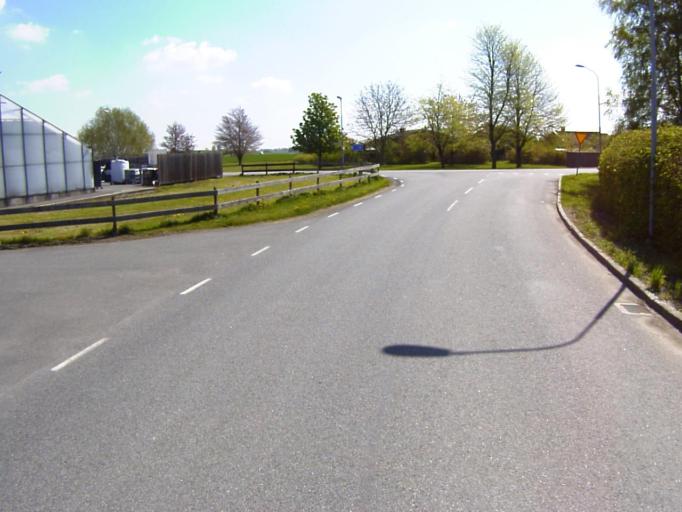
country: SE
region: Skane
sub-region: Kristianstads Kommun
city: Fjalkinge
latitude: 56.0175
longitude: 14.2325
